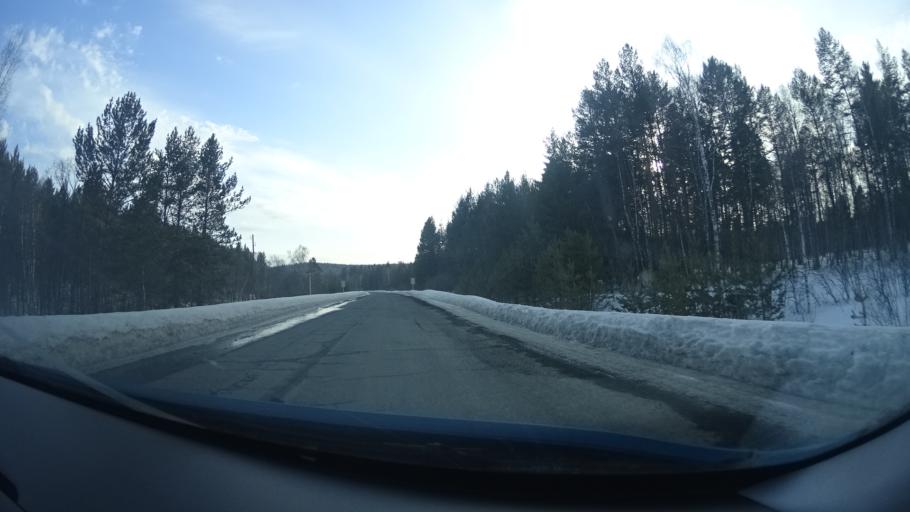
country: RU
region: Bashkortostan
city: Lomovka
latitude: 53.6464
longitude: 58.2015
